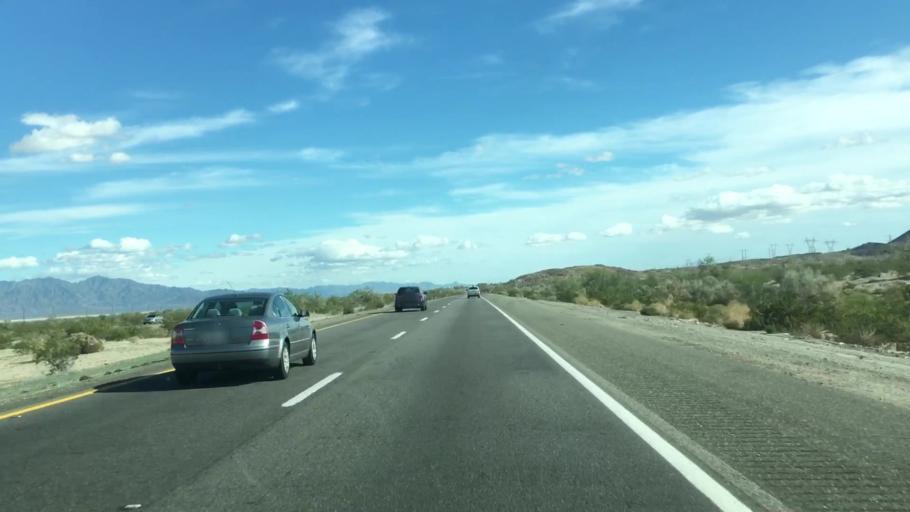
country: US
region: California
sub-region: Imperial County
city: Niland
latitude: 33.7081
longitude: -115.3606
